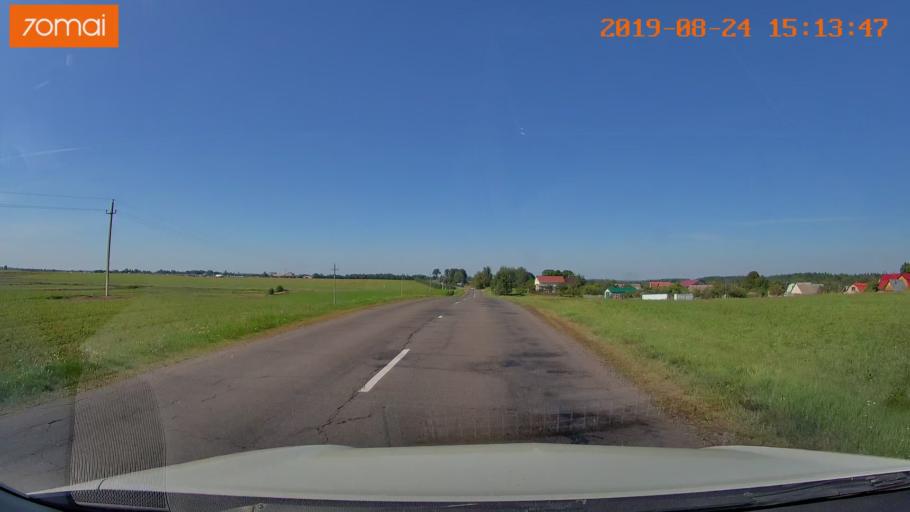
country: BY
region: Minsk
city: Samakhvalavichy
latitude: 53.6172
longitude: 27.5748
